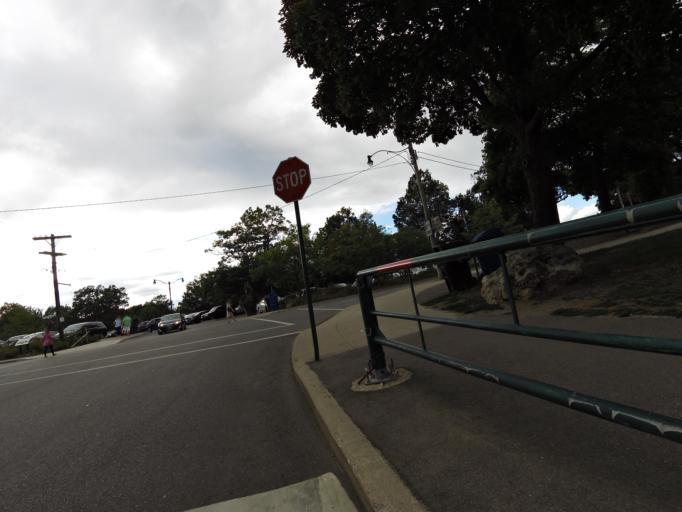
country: CA
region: Ontario
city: Toronto
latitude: 43.6456
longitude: -79.4645
